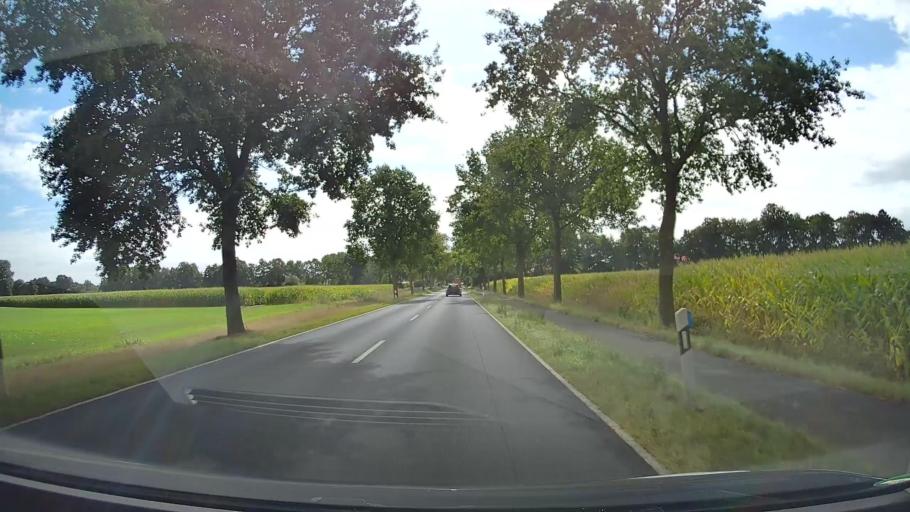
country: DE
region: Lower Saxony
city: Rhade
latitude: 53.3338
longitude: 9.1106
